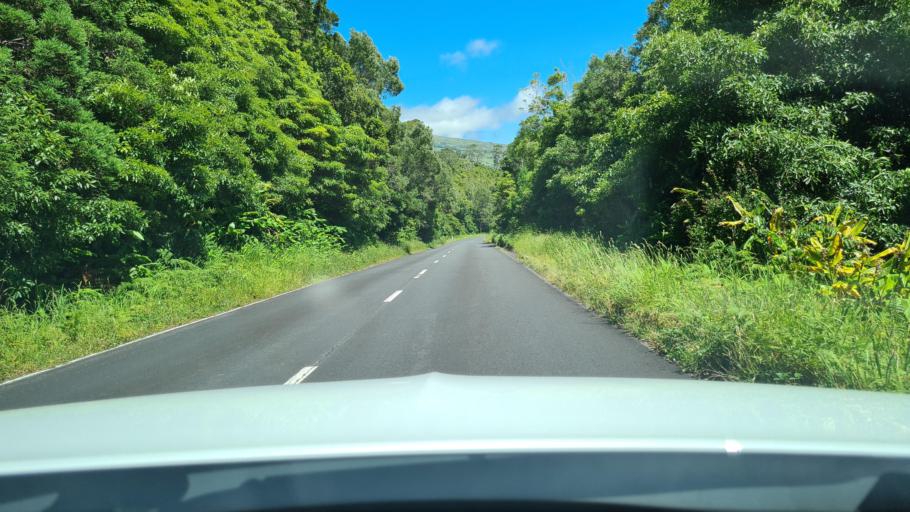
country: PT
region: Azores
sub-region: Sao Roque do Pico
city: Sao Roque do Pico
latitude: 38.4262
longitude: -28.2876
